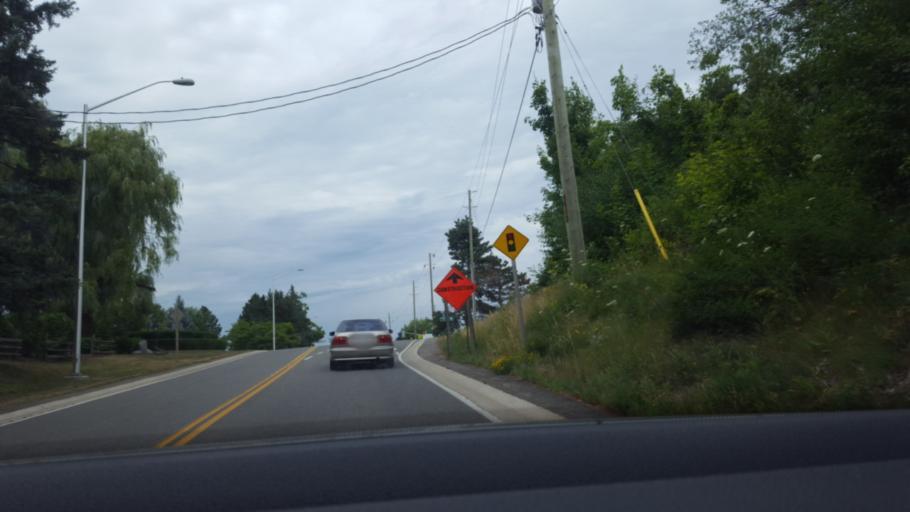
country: CA
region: Ontario
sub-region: Halton
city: Milton
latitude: 43.5866
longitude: -79.8692
